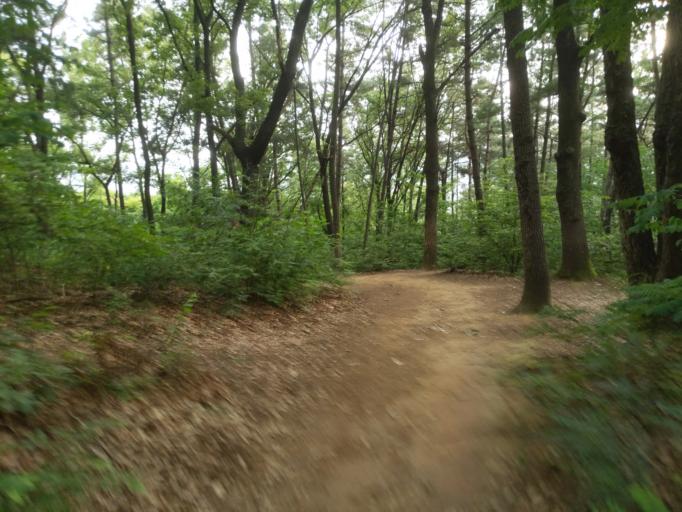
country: KR
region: Daegu
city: Hwawon
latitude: 35.7999
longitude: 128.5269
